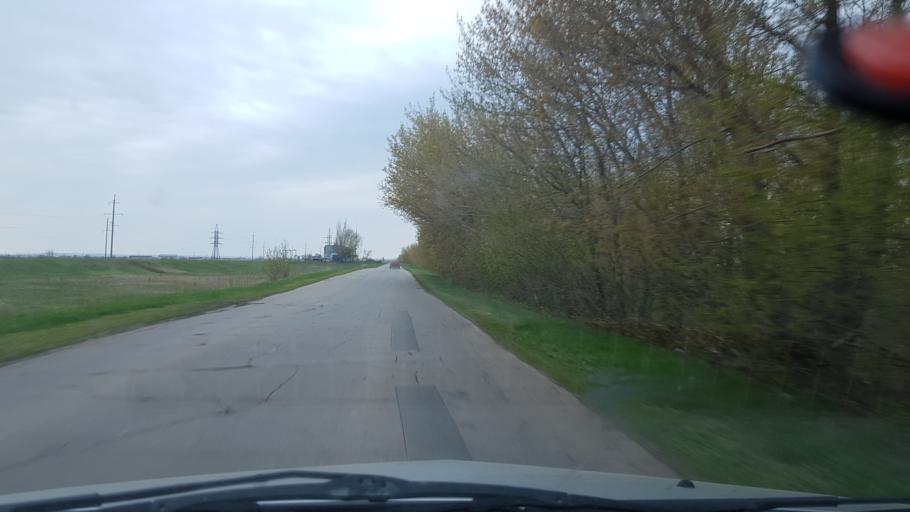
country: RU
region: Samara
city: Khryashchevka
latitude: 53.6702
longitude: 49.1141
